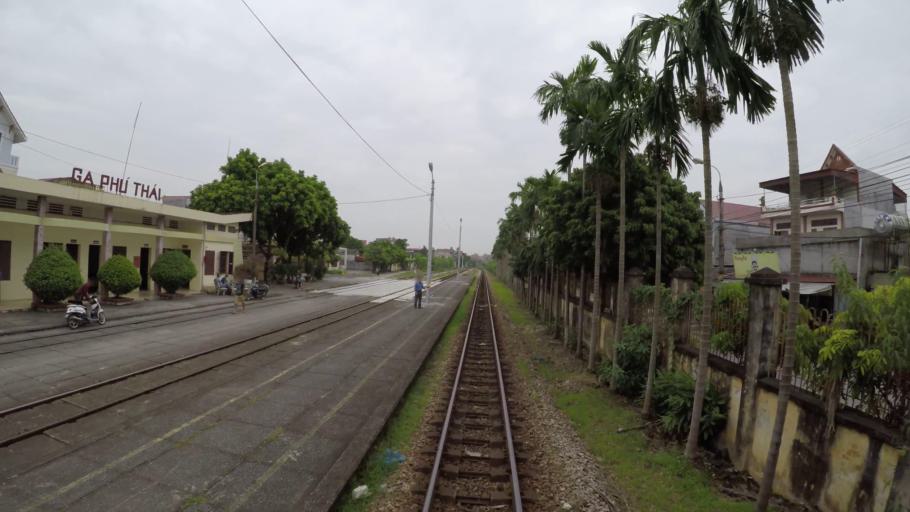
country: VN
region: Hai Duong
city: Phu Thai
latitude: 20.9729
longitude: 106.4867
